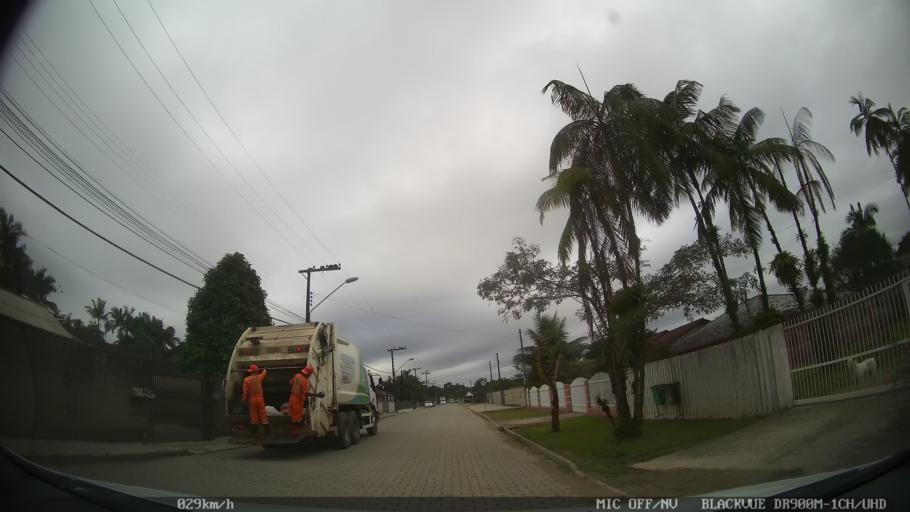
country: BR
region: Santa Catarina
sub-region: Joinville
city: Joinville
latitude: -26.2662
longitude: -48.9267
